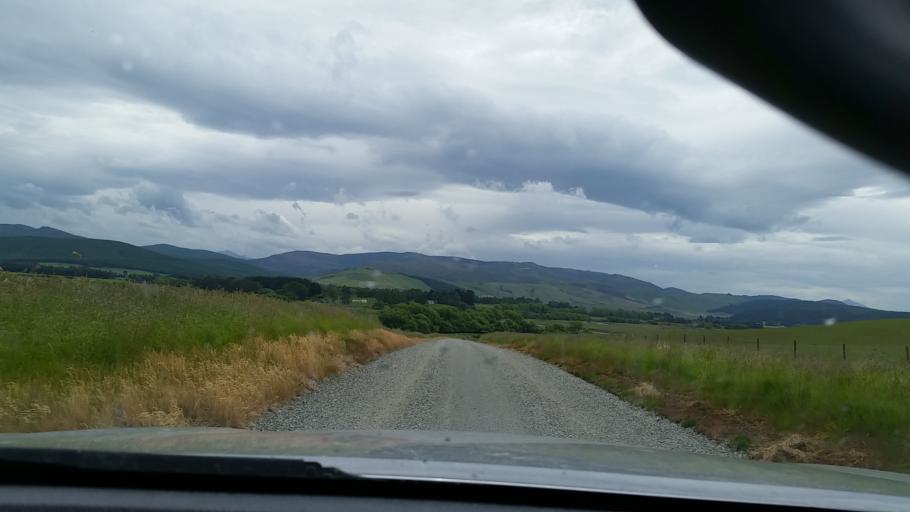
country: NZ
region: Southland
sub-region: Southland District
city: Winton
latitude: -45.8631
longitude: 168.1408
